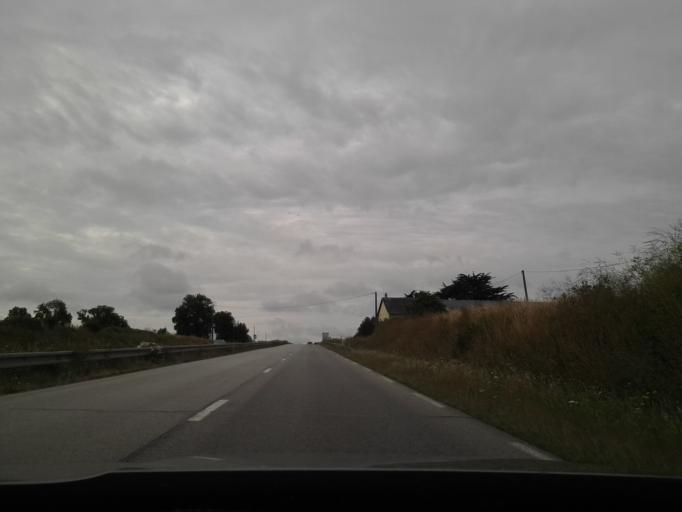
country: FR
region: Lower Normandy
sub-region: Departement de la Manche
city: Sainte-Mere-Eglise
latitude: 49.3858
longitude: -1.3002
